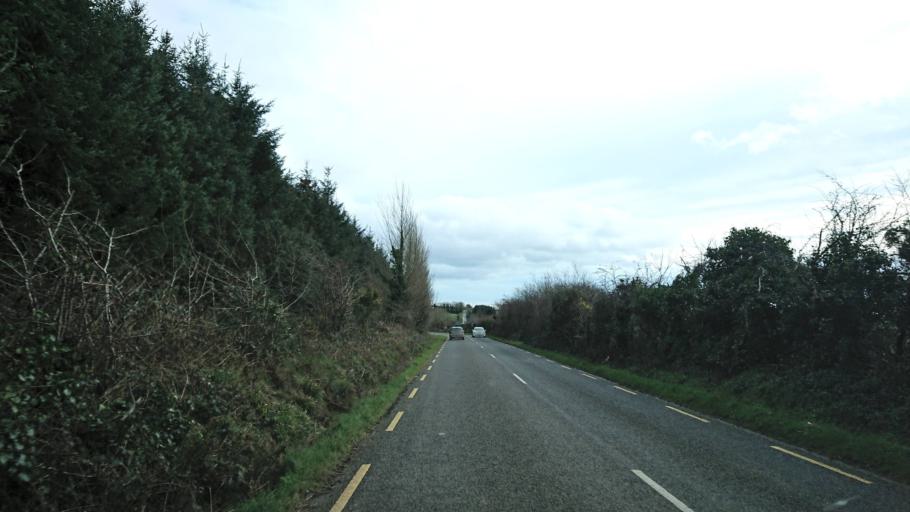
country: IE
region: Munster
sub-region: Waterford
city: Dunmore East
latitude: 52.2419
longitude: -6.8926
